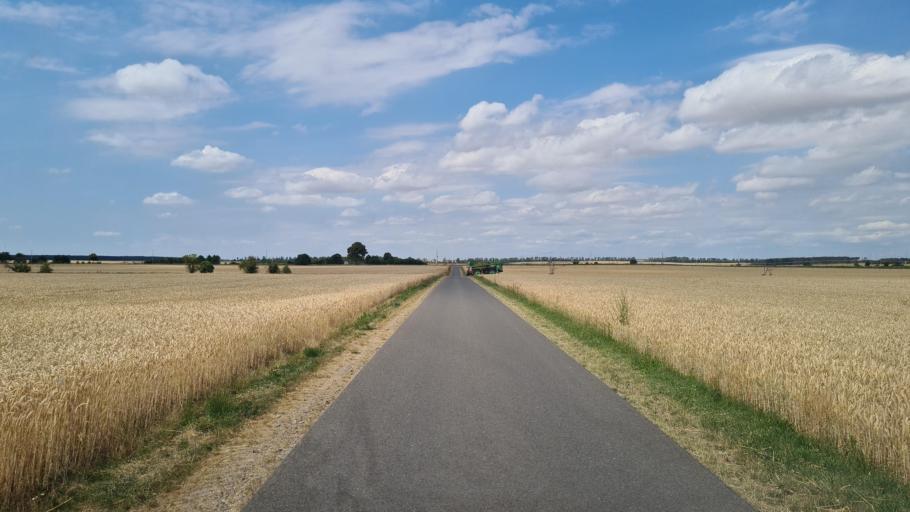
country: DE
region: Brandenburg
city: Juterbog
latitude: 51.9515
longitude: 13.0472
